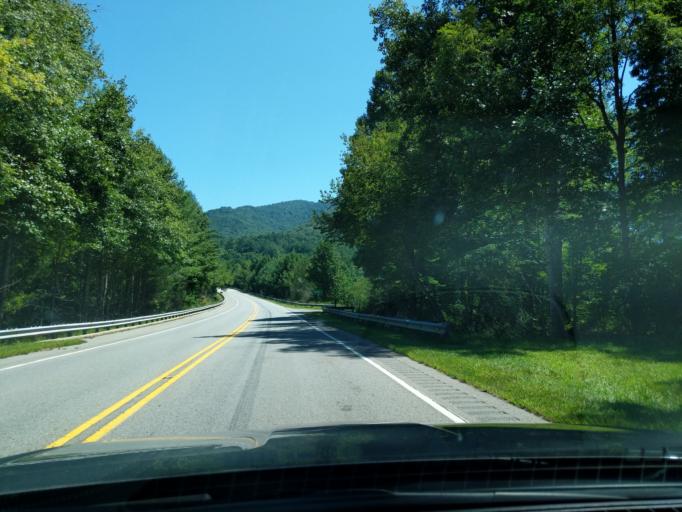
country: US
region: North Carolina
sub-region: Macon County
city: Franklin
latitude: 35.1377
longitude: -83.4923
